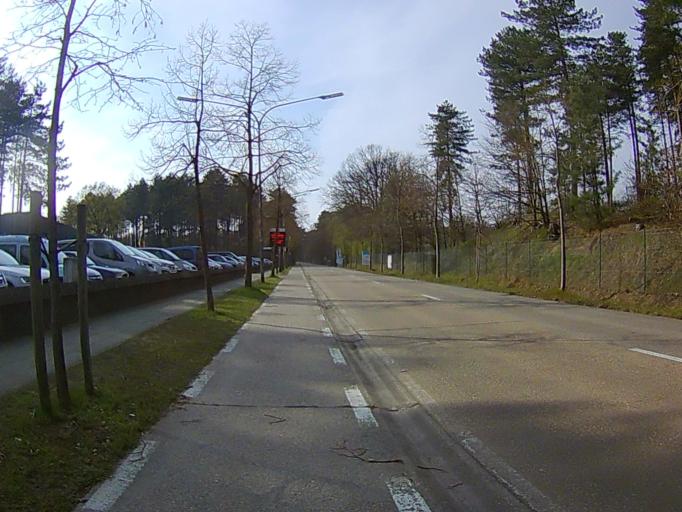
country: BE
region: Flanders
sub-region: Provincie Antwerpen
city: Herentals
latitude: 51.1884
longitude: 4.8309
